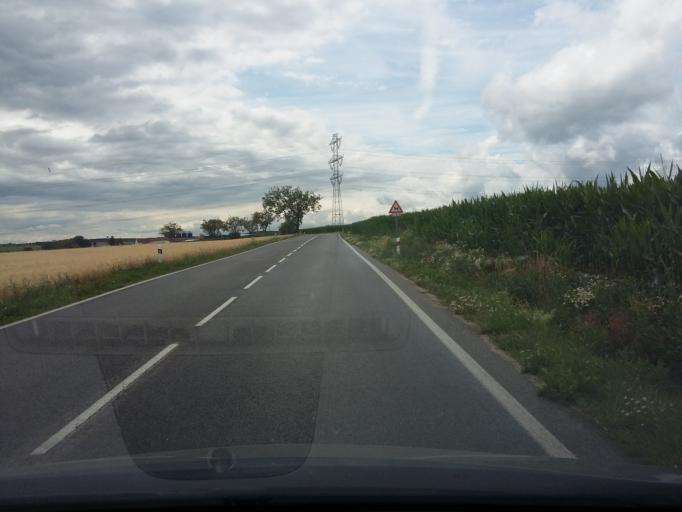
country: SK
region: Trnavsky
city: Vrbove
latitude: 48.6013
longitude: 17.6942
